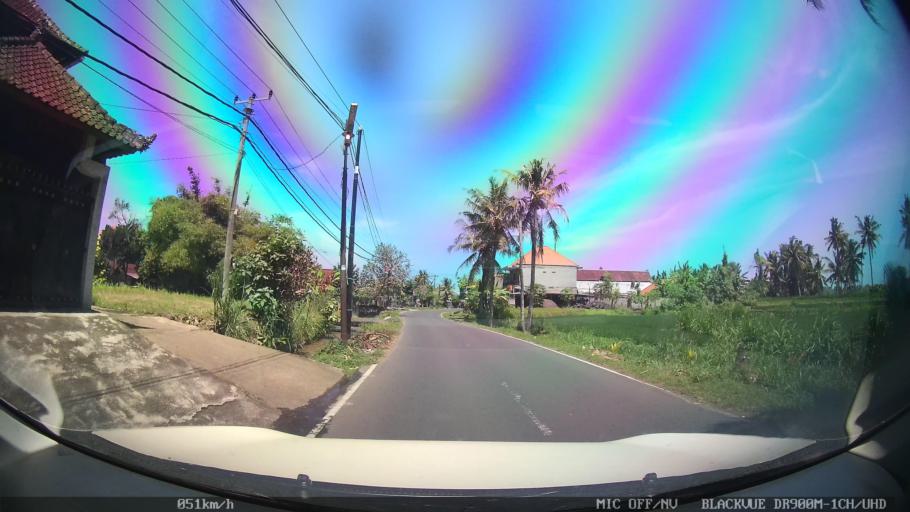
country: ID
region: Bali
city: Klungkung
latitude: -8.5779
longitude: 115.3384
